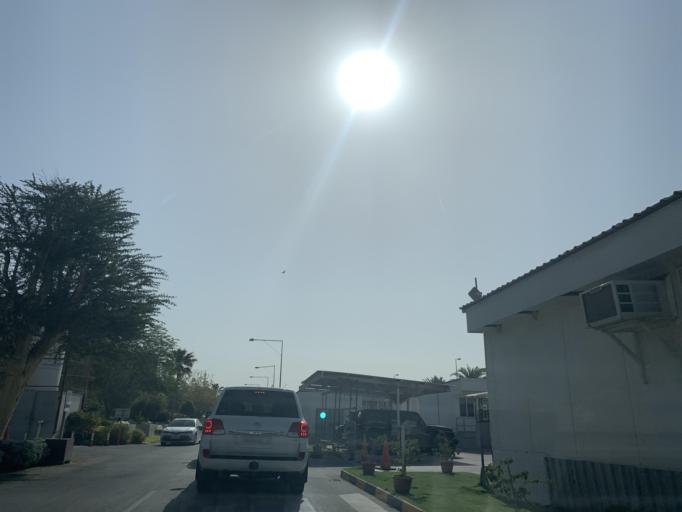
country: BH
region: Muharraq
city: Al Muharraq
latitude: 26.2613
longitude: 50.6001
